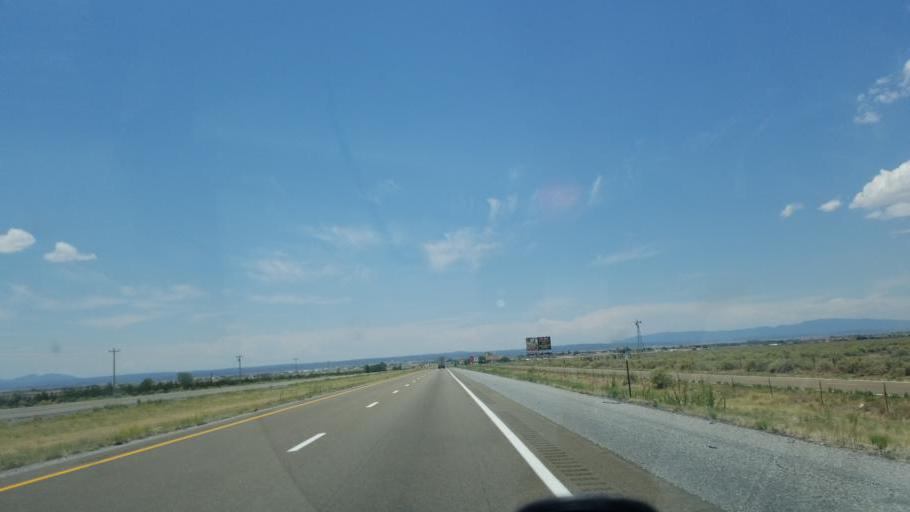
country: US
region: New Mexico
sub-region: Torrance County
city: Moriarty
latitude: 35.0049
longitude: -105.9860
